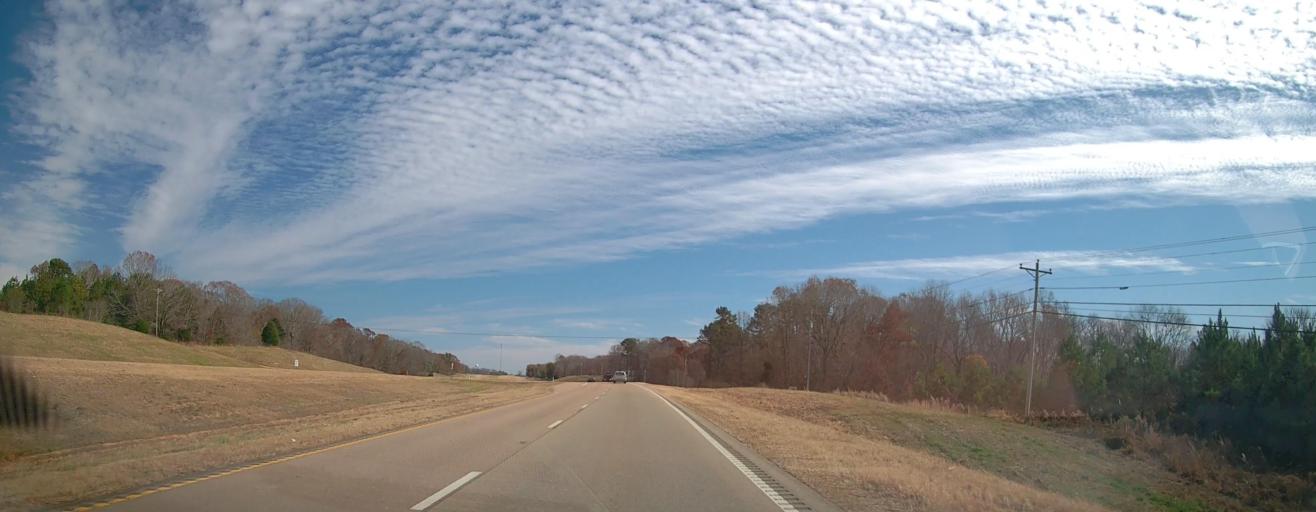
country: US
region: Mississippi
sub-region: Tippah County
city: Ripley
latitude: 34.9506
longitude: -88.8268
